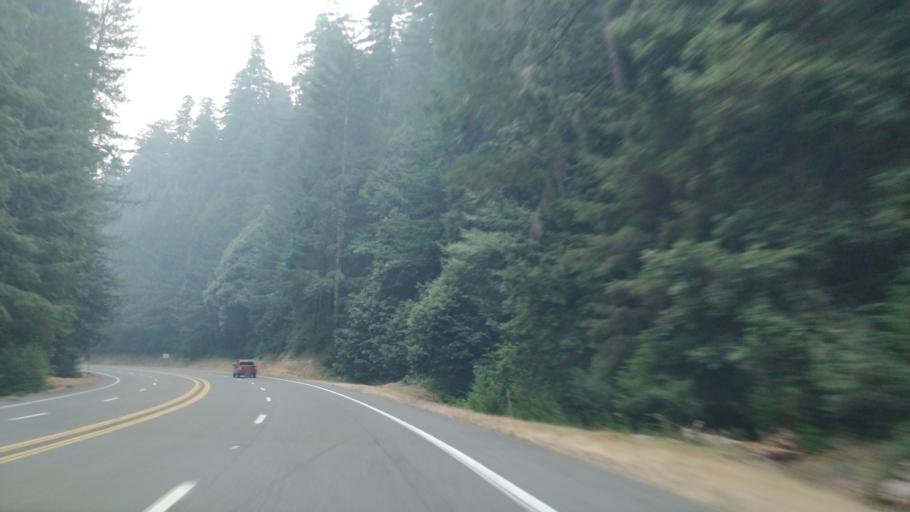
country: US
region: California
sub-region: Humboldt County
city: Rio Dell
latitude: 40.3712
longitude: -123.9265
